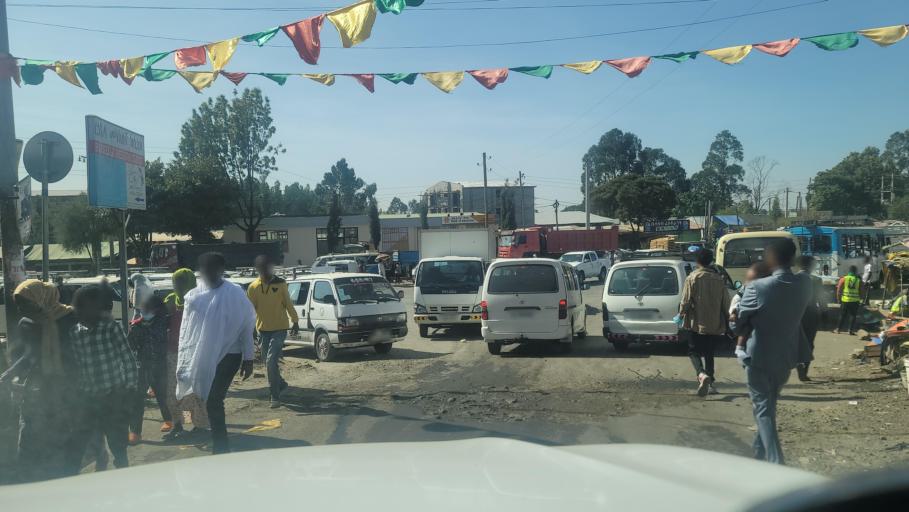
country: ET
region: Adis Abeba
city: Addis Ababa
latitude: 9.0378
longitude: 38.8314
